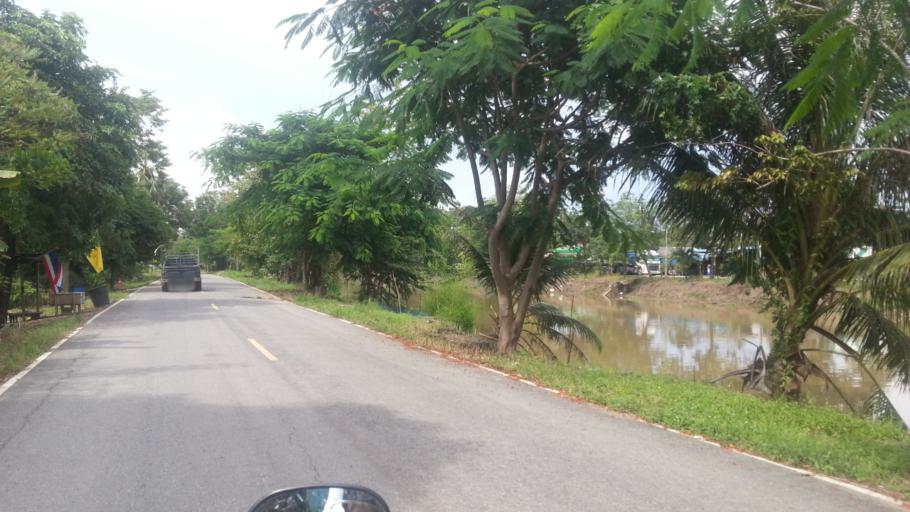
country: TH
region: Pathum Thani
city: Nong Suea
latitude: 14.0831
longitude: 100.8237
